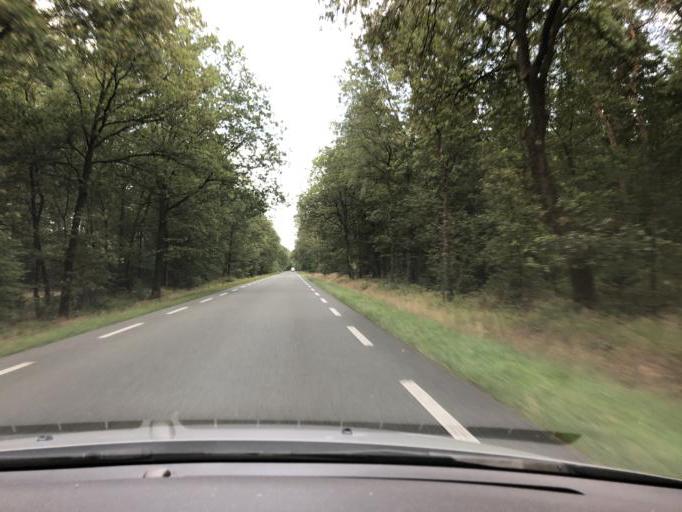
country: NL
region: Drenthe
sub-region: Gemeente Borger-Odoorn
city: Borger
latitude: 52.9364
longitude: 6.7426
